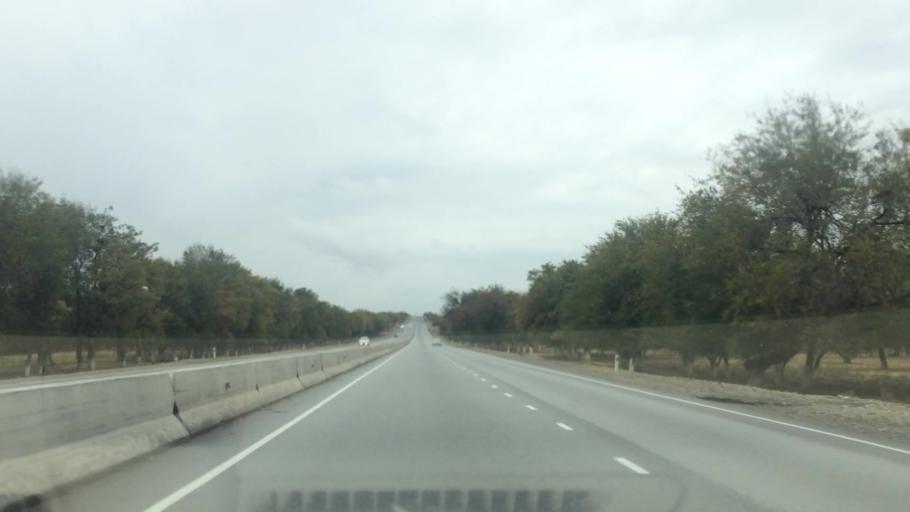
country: UZ
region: Samarqand
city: Bulung'ur
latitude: 39.8713
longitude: 67.4785
